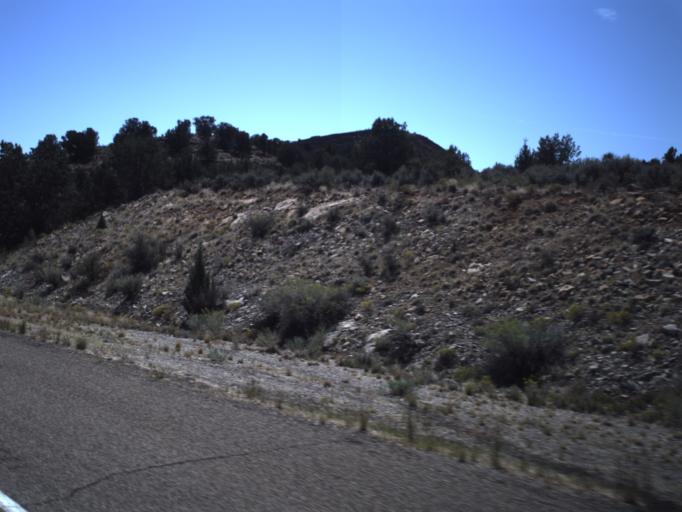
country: US
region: Utah
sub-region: Washington County
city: Ivins
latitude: 37.2520
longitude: -113.6297
